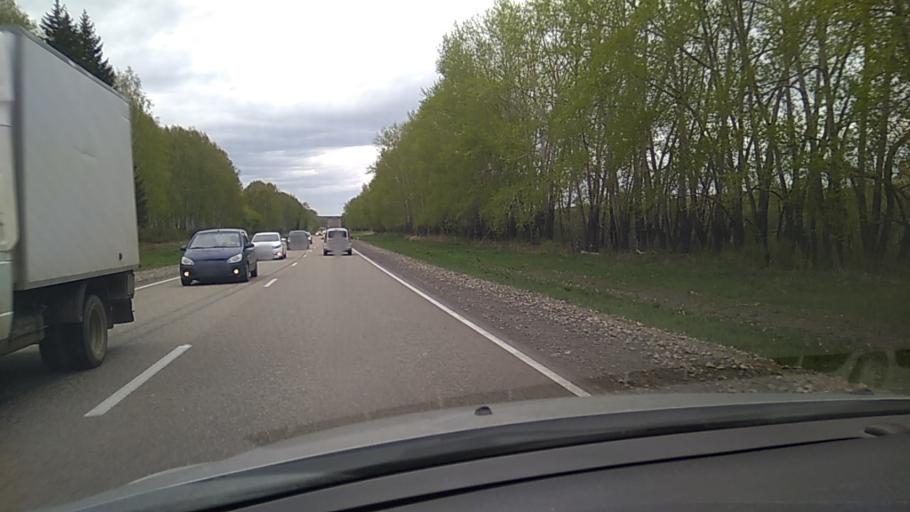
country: RU
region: Sverdlovsk
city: Dvurechensk
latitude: 56.6531
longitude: 61.1907
